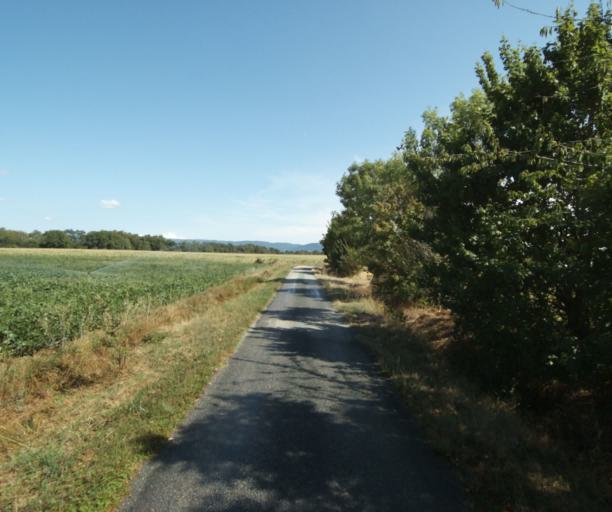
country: FR
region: Midi-Pyrenees
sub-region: Departement de la Haute-Garonne
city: Revel
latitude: 43.4889
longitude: 1.9715
